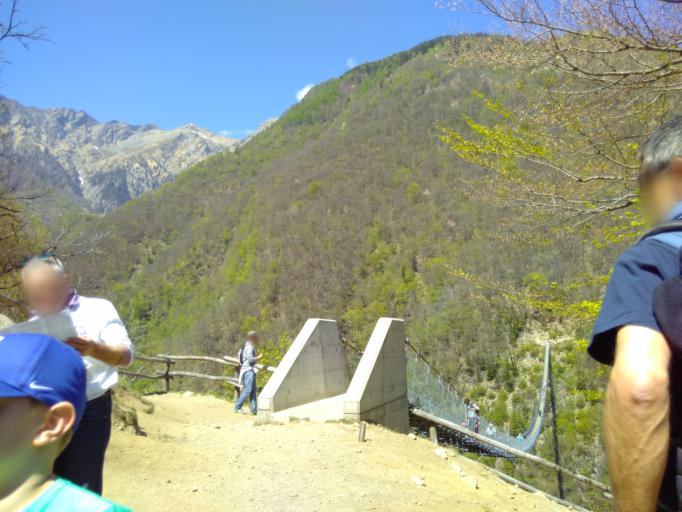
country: CH
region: Ticino
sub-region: Bellinzona District
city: Sementina
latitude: 46.1936
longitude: 8.9744
